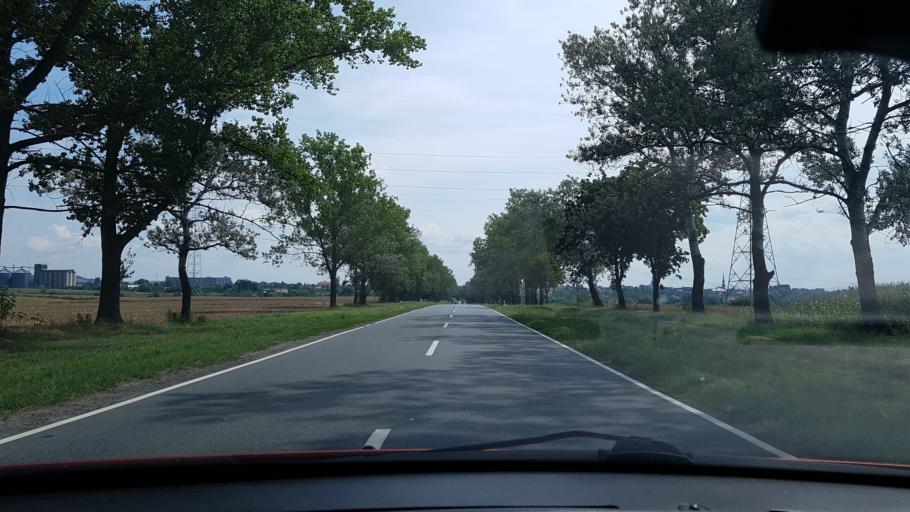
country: PL
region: Lower Silesian Voivodeship
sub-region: Powiat zabkowicki
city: Zabkowice Slaskie
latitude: 50.6044
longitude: 16.7941
